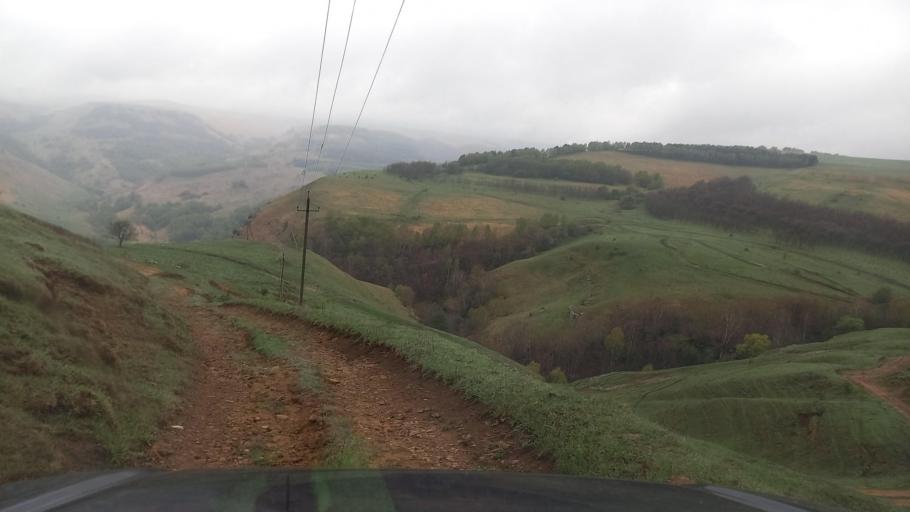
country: RU
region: Stavropol'skiy
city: Nezhinskiy
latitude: 43.8581
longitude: 42.6389
